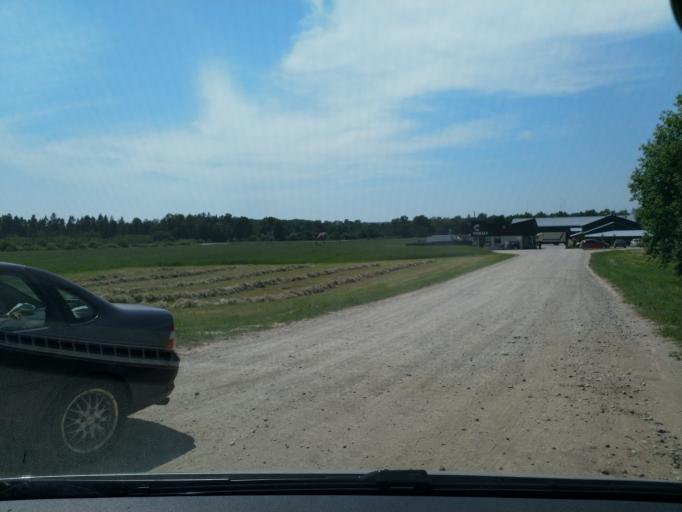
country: LV
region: Kuldigas Rajons
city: Kuldiga
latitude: 56.9559
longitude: 22.0137
